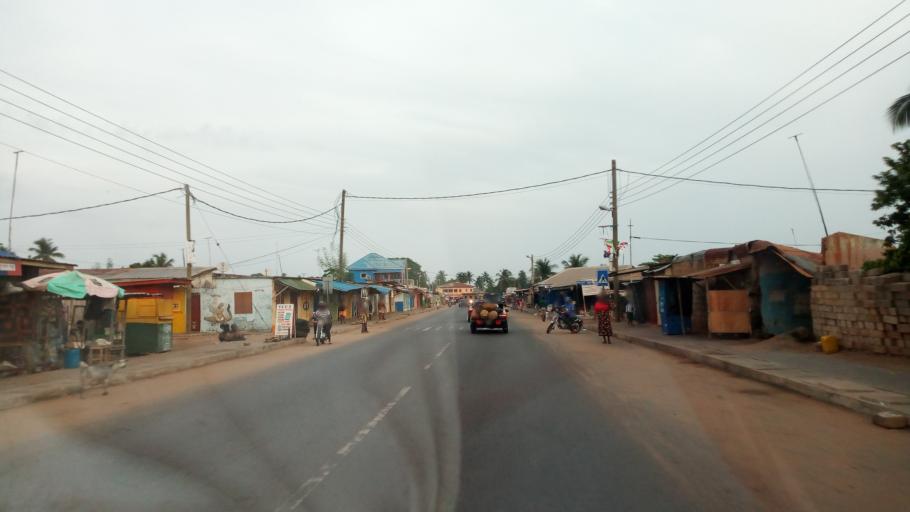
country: TG
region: Maritime
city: Lome
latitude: 6.1205
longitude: 1.1870
